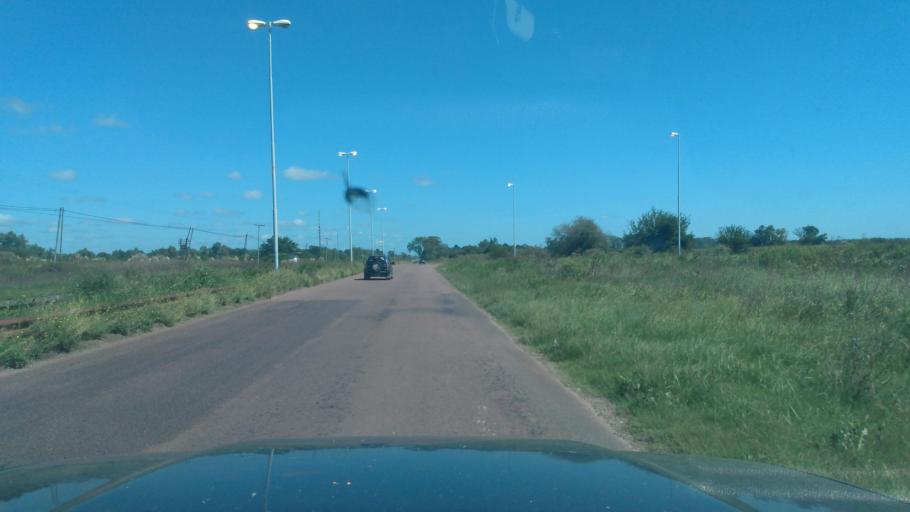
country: AR
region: Buenos Aires
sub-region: Partido de Lujan
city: Lujan
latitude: -34.5882
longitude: -59.0395
